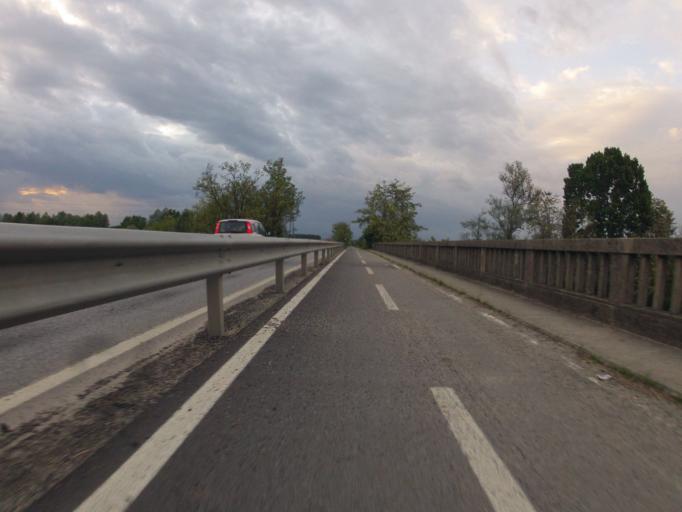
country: IT
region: Piedmont
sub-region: Provincia di Torino
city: Villafranca Piemonte
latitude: 44.8121
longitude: 7.4992
